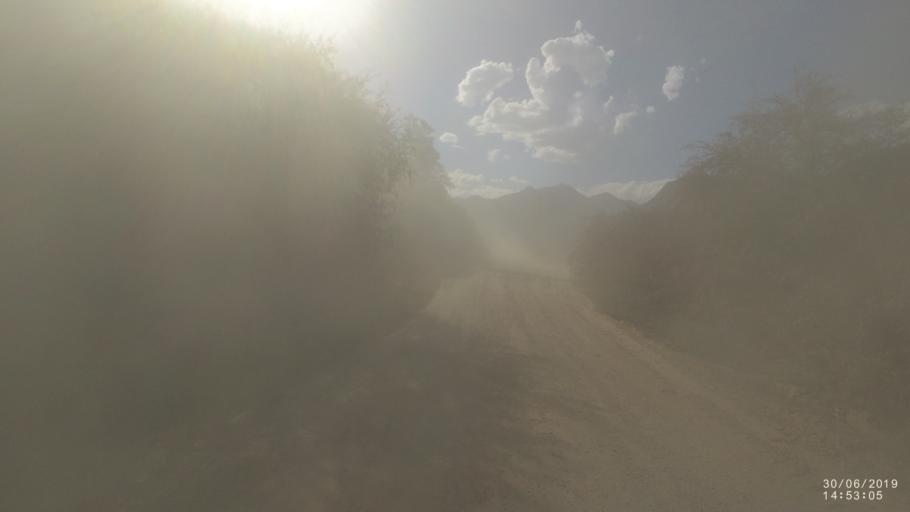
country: BO
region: Cochabamba
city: Irpa Irpa
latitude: -17.7659
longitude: -66.3479
